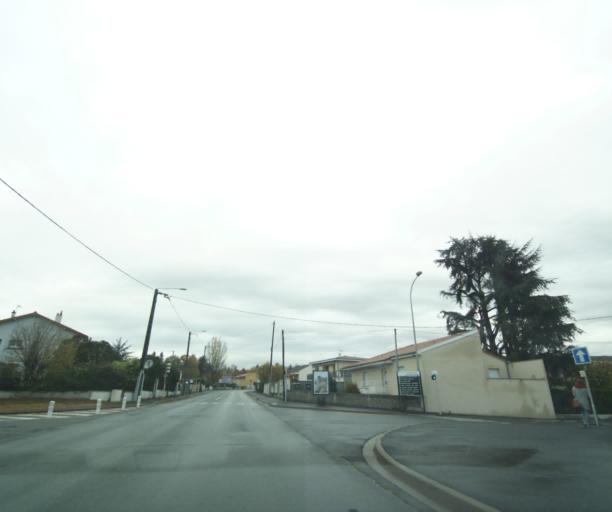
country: FR
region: Auvergne
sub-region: Departement du Puy-de-Dome
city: Cournon-d'Auvergne
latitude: 45.7349
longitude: 3.2074
